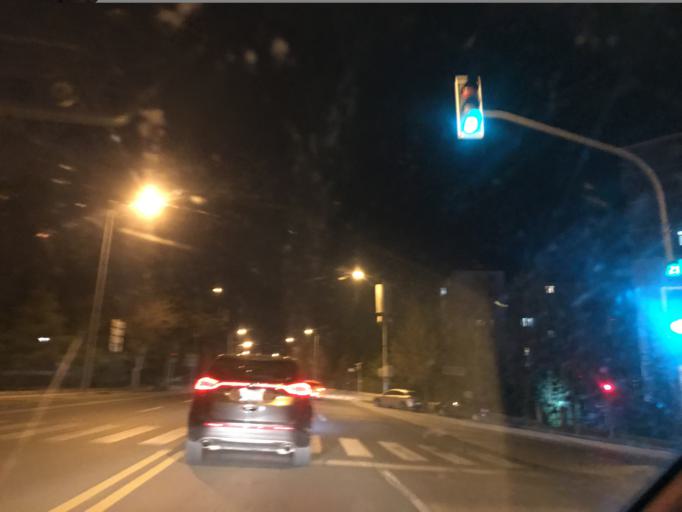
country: TR
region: Ankara
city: Cankaya
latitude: 39.8790
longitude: 32.8653
